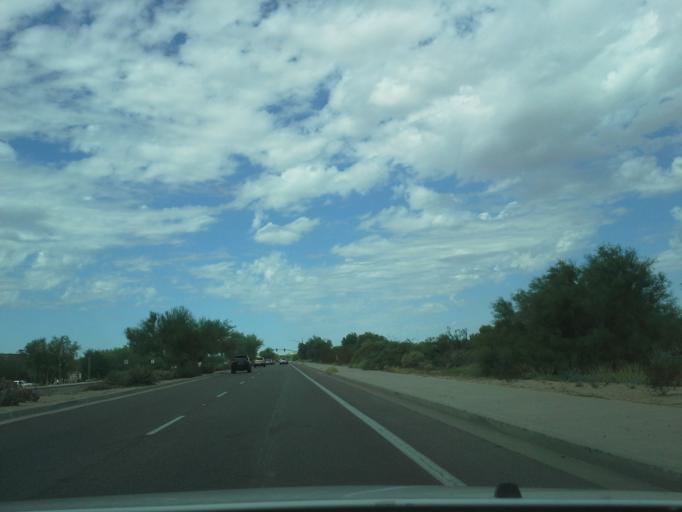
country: US
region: Arizona
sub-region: Maricopa County
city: Paradise Valley
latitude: 33.6402
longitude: -111.8816
